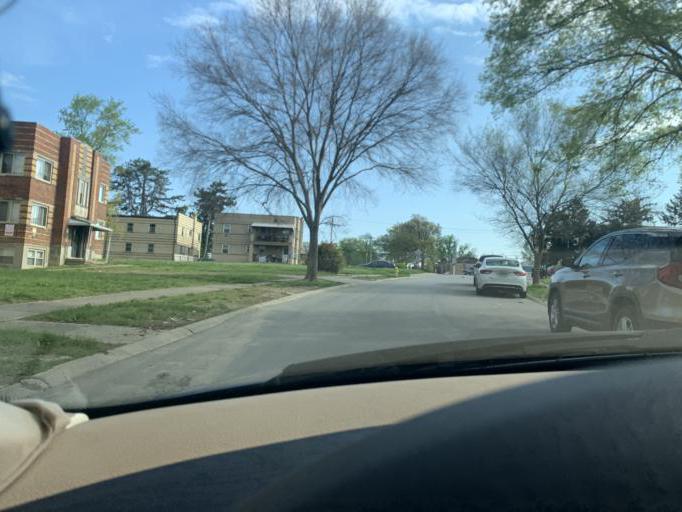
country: US
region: Ohio
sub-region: Hamilton County
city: Golf Manor
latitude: 39.1912
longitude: -84.4567
